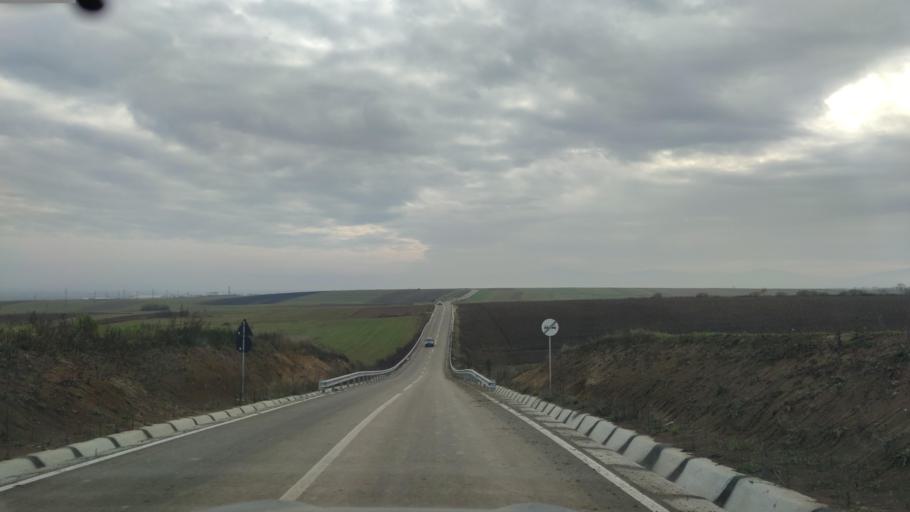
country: RO
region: Harghita
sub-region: Comuna Subcetate
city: Subcetate
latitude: 46.8257
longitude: 25.4452
